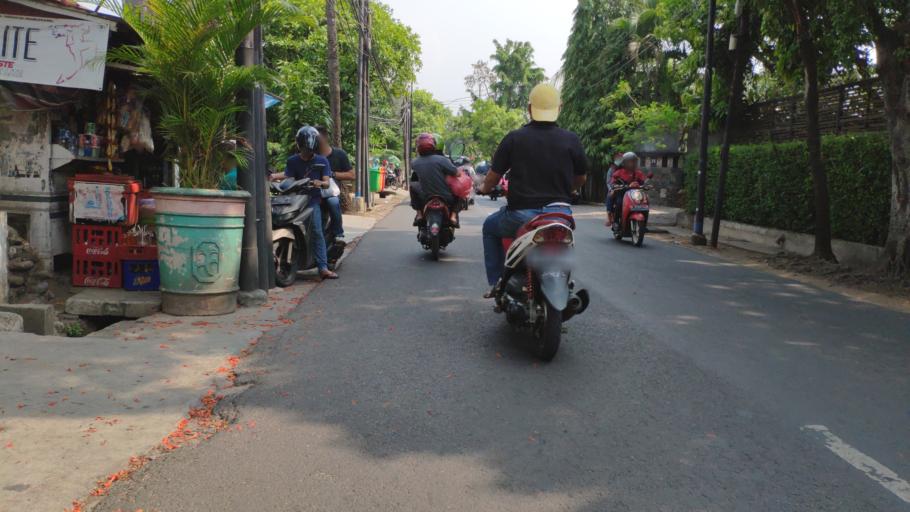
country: ID
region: Jakarta Raya
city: Jakarta
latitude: -6.2630
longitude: 106.8237
